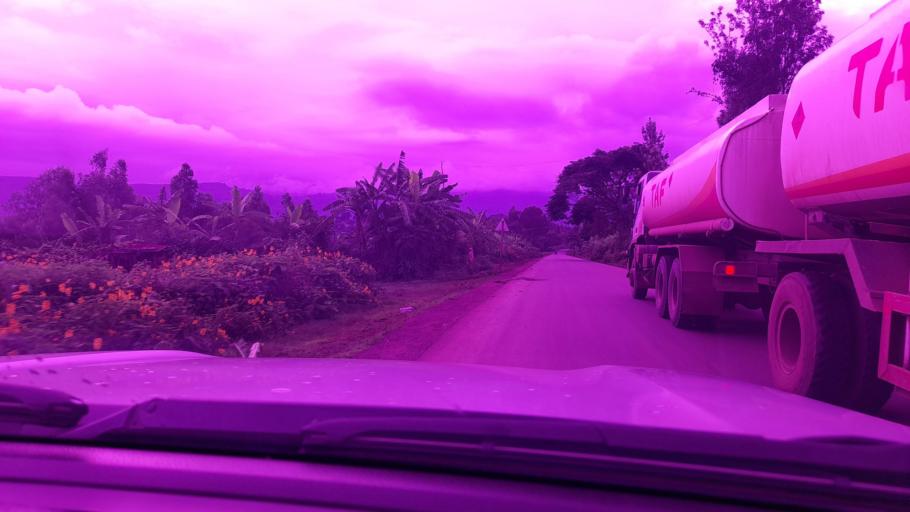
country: ET
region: Oromiya
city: Jima
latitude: 7.8896
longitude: 37.3905
